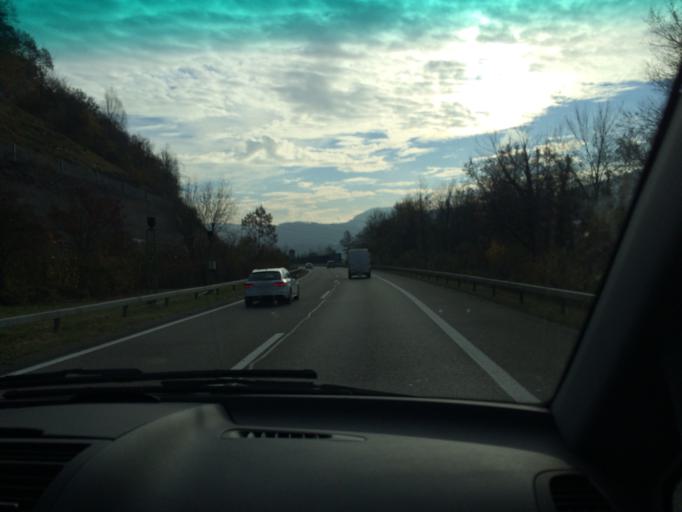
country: CH
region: Basel-Landschaft
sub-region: Bezirk Sissach
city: Itingen
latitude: 47.4752
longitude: 7.7812
